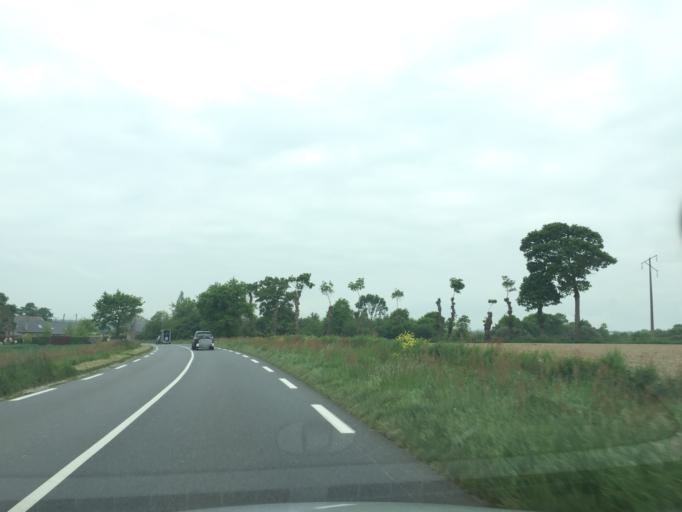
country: FR
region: Brittany
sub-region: Departement des Cotes-d'Armor
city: Henanbihen
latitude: 48.5178
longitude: -2.4447
